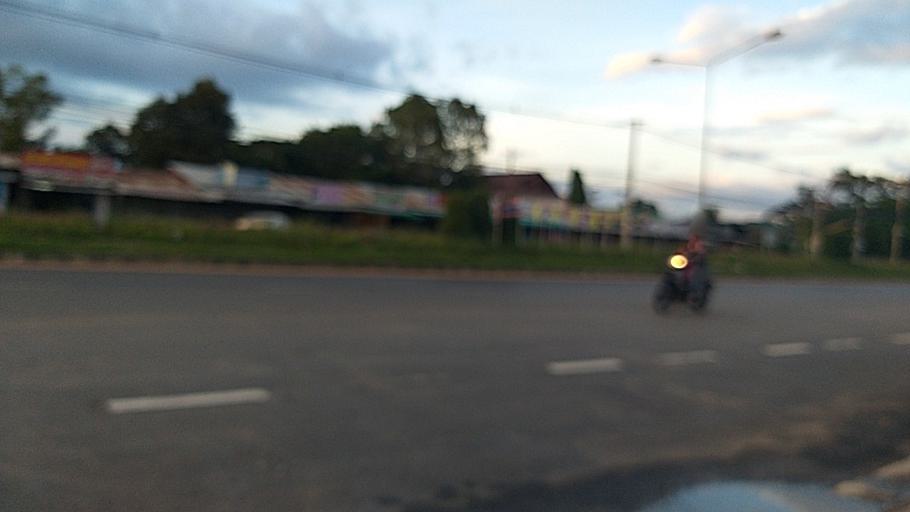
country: TH
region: Surin
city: Kap Choeng
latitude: 14.4531
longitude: 103.6901
